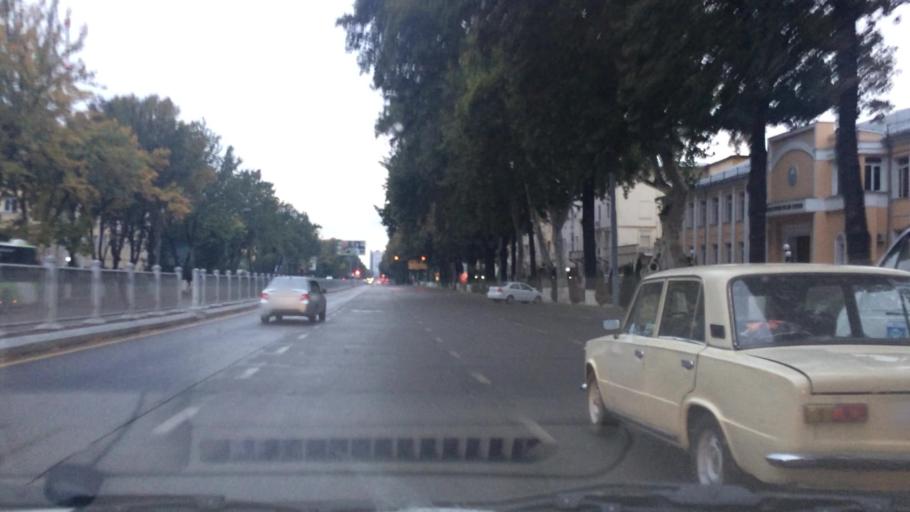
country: UZ
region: Toshkent Shahri
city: Tashkent
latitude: 41.3206
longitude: 69.2633
